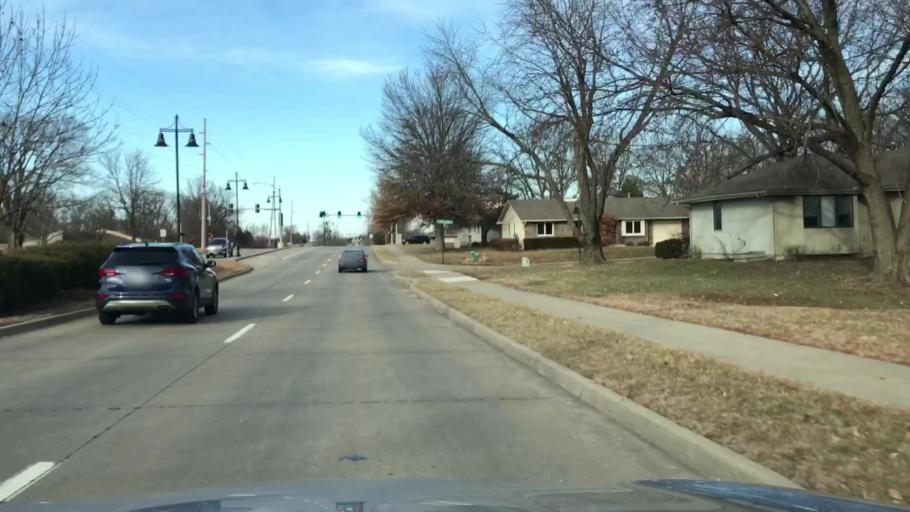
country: US
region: Missouri
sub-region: Jackson County
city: Lees Summit
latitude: 38.9187
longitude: -94.4130
